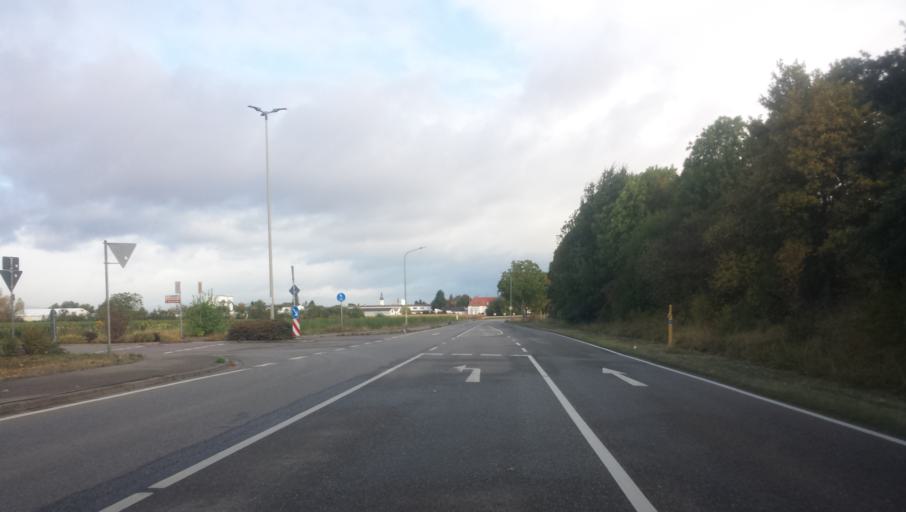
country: DE
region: Rheinland-Pfalz
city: Bohl-Iggelheim
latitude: 49.3744
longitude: 8.3070
